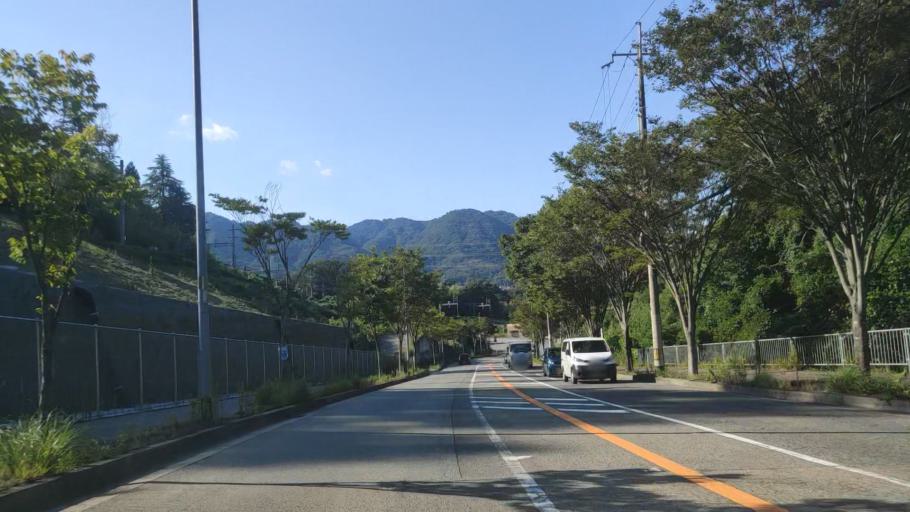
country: JP
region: Hyogo
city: Kobe
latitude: 34.7751
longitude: 135.1940
